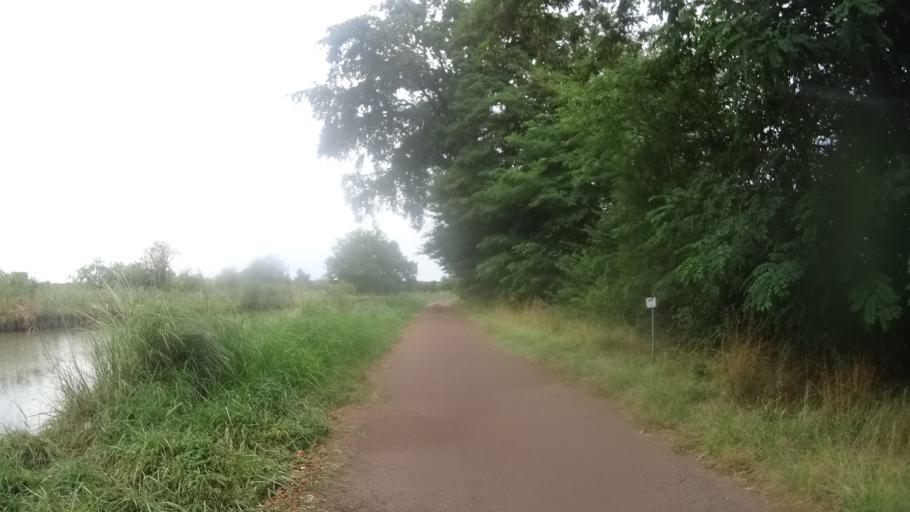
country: FR
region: Bourgogne
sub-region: Departement de la Nievre
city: Imphy
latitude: 46.8677
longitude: 3.2777
